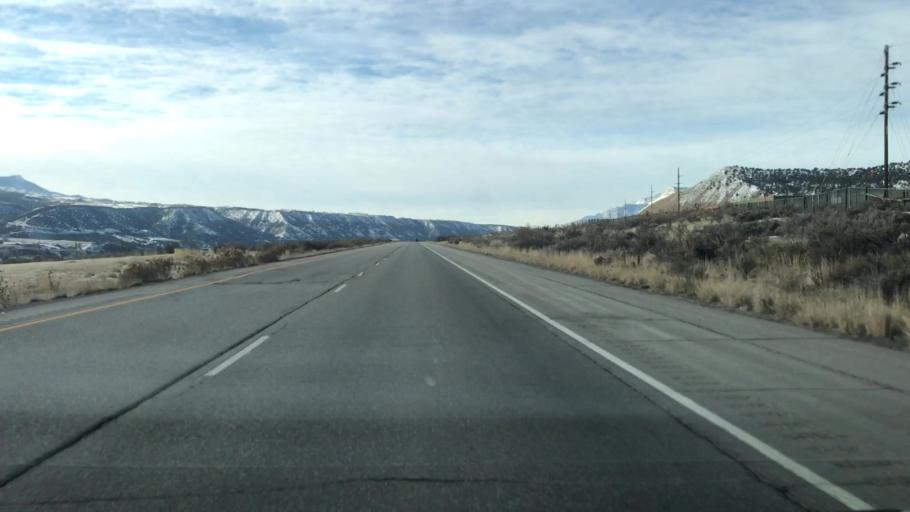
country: US
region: Colorado
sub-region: Garfield County
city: Battlement Mesa
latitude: 39.4945
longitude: -107.9469
